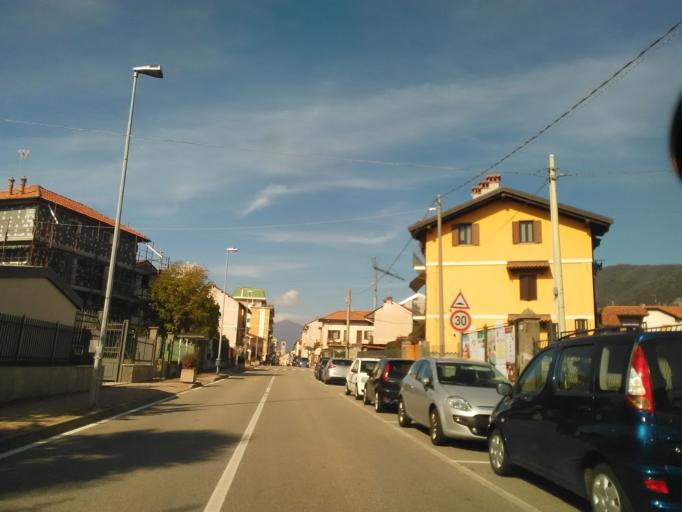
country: IT
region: Piedmont
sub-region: Provincia di Vercelli
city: Serravalle Sesia
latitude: 45.6813
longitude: 8.3160
